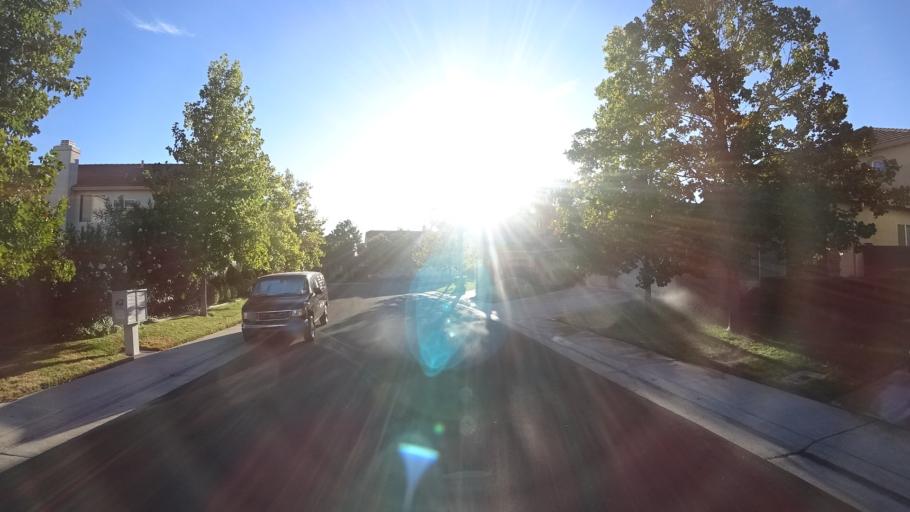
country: US
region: California
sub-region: Sacramento County
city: Laguna
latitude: 38.3957
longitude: -121.4794
